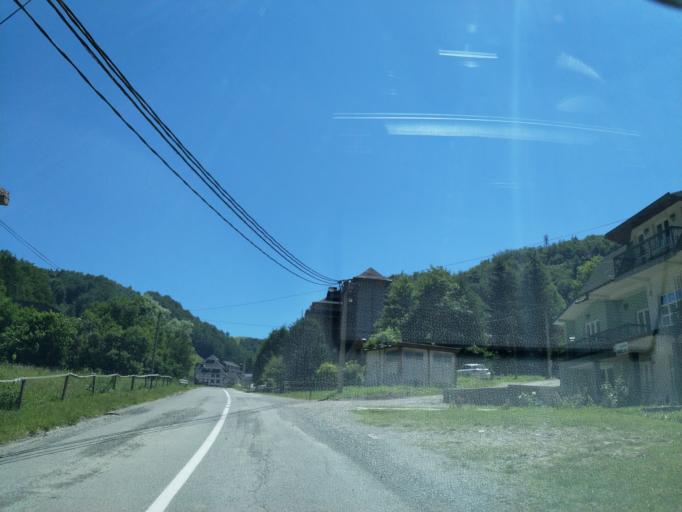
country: XK
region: Mitrovica
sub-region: Komuna e Leposaviqit
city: Leposaviq
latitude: 43.2941
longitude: 20.8794
